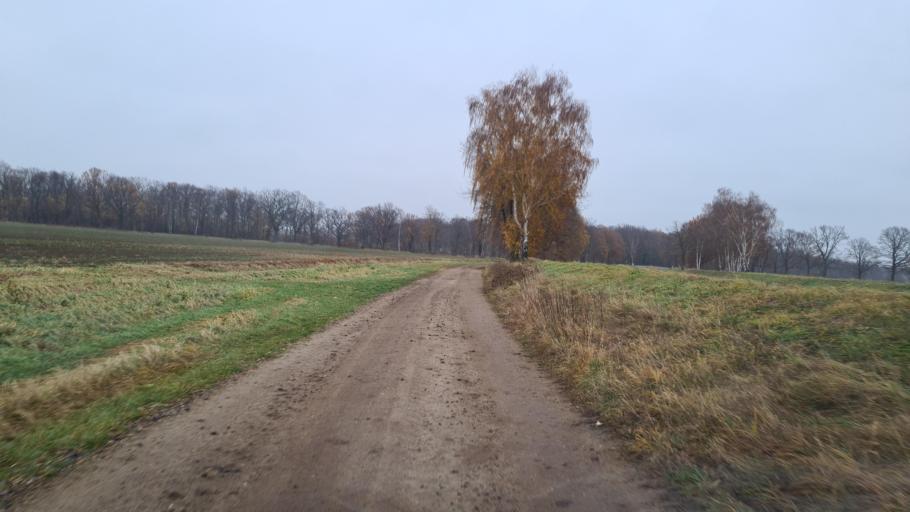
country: DE
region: Brandenburg
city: Lindenau
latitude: 51.4036
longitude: 13.7036
